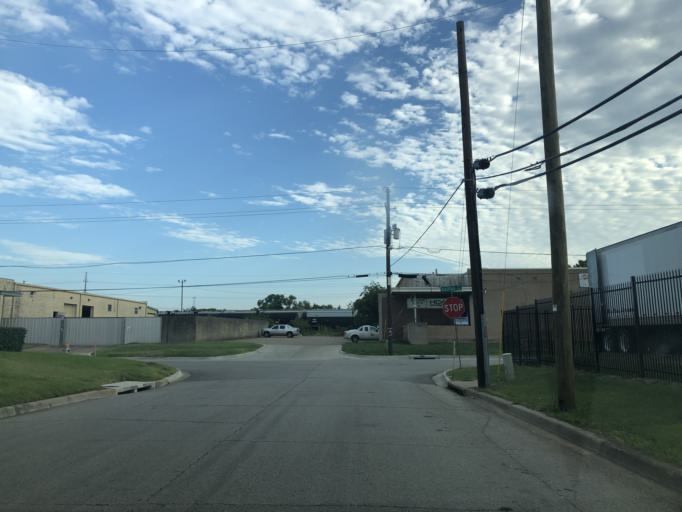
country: US
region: Texas
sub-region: Dallas County
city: Irving
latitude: 32.8121
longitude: -96.8822
